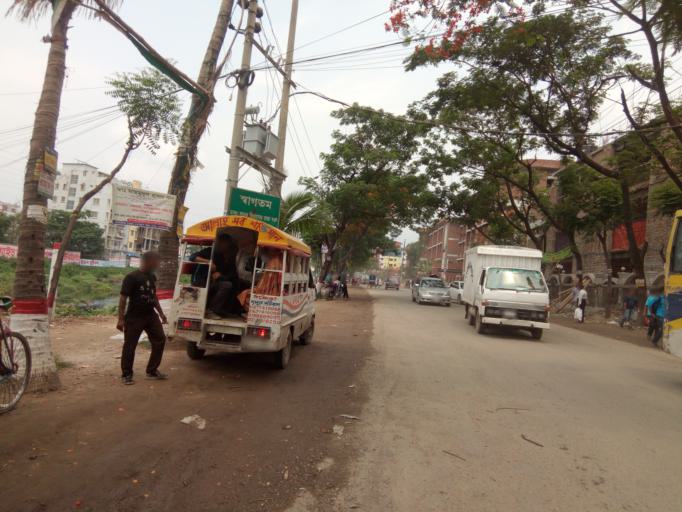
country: BD
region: Dhaka
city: Paltan
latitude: 23.7638
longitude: 90.4312
